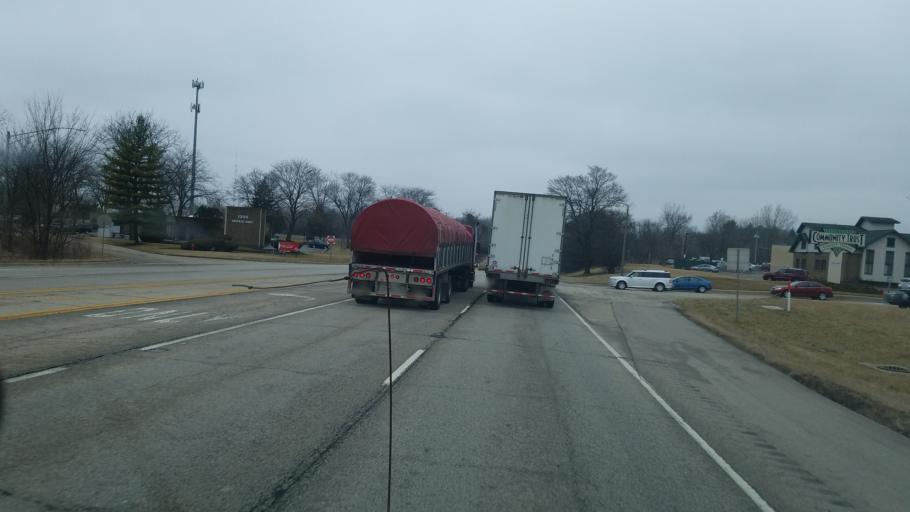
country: US
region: Illinois
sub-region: Lake County
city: Gurnee
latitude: 42.3784
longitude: -87.9093
